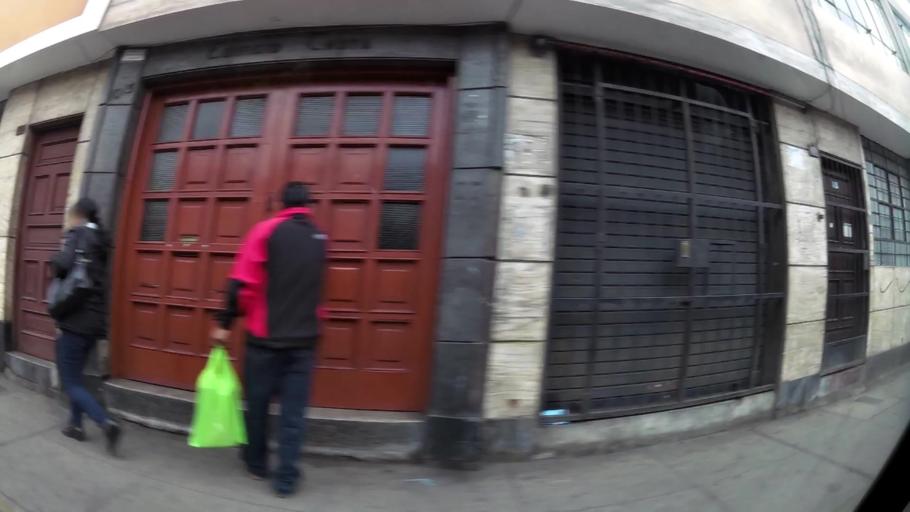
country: PE
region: Lima
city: Lima
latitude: -12.0526
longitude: -77.0408
